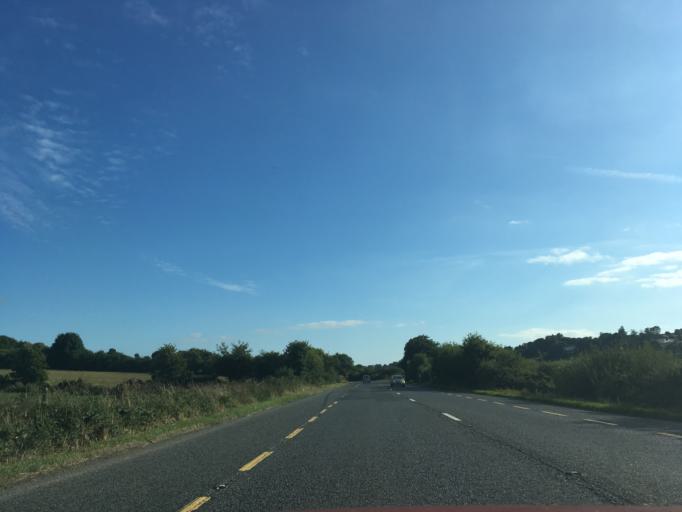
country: IE
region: Munster
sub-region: Waterford
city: Waterford
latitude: 52.3384
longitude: -7.0538
